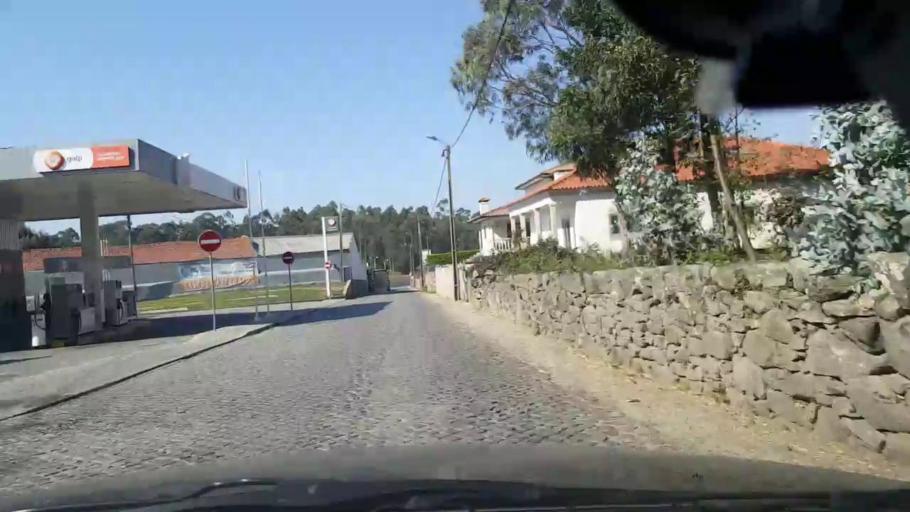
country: PT
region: Porto
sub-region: Vila do Conde
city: Arvore
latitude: 41.3851
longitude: -8.6858
